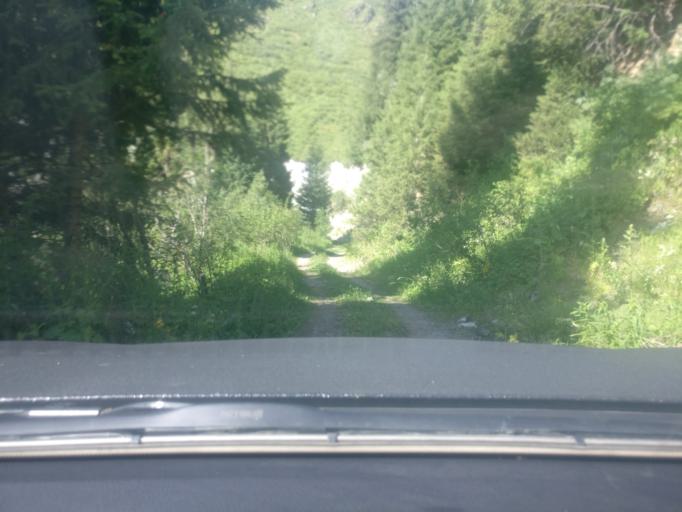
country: KZ
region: Almaty Qalasy
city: Almaty
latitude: 43.1065
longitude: 76.9534
